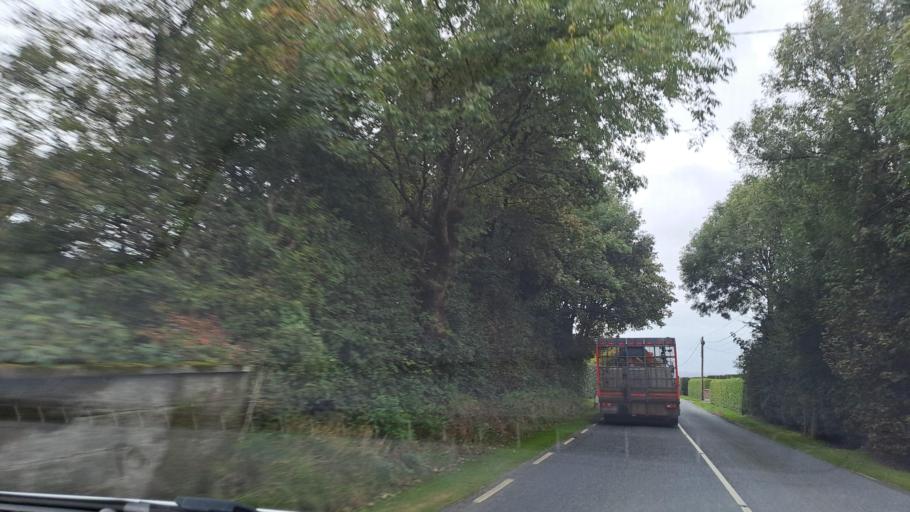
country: IE
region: Ulster
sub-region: County Monaghan
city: Castleblayney
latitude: 54.0883
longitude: -6.8304
